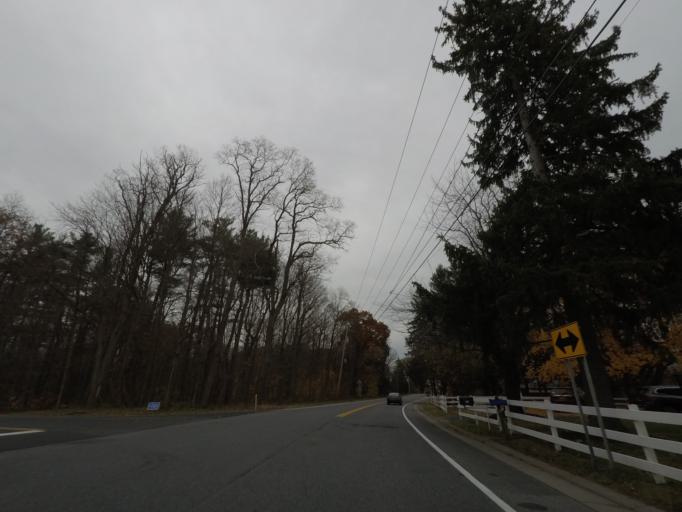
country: US
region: New York
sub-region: Saratoga County
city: Country Knolls
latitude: 42.8934
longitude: -73.8501
